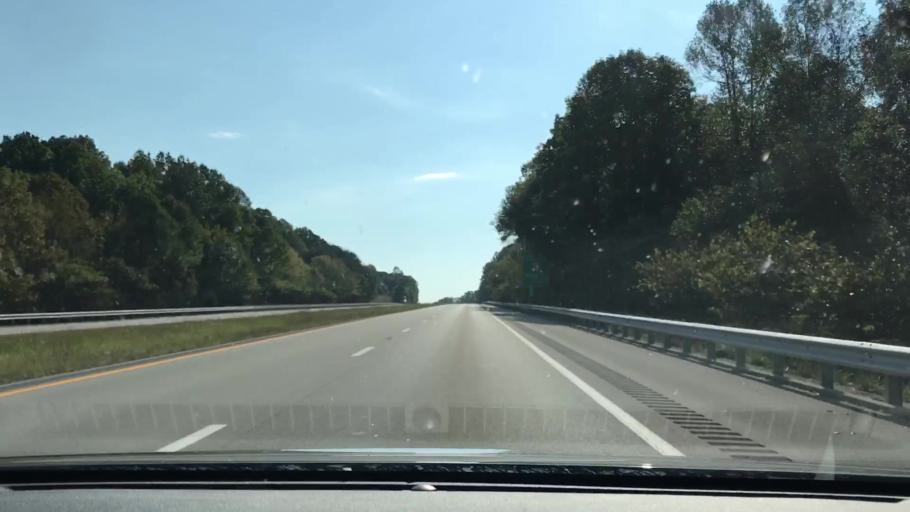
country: US
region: Kentucky
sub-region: Pulaski County
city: Somerset
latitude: 37.0952
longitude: -84.8251
